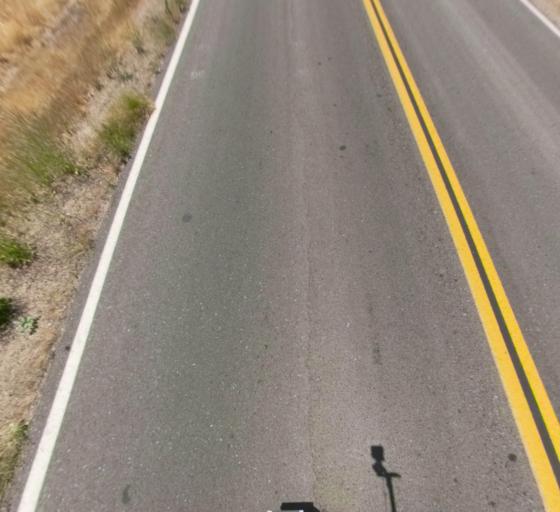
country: US
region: California
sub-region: Madera County
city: Bonadelle Ranchos-Madera Ranchos
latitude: 37.0025
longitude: -119.8937
